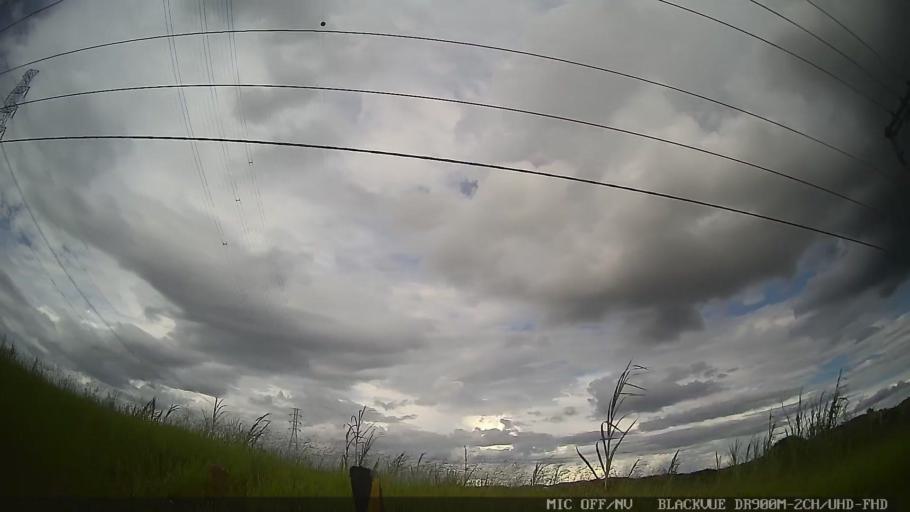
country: BR
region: Sao Paulo
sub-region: Mogi das Cruzes
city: Mogi das Cruzes
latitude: -23.5329
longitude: -46.1558
